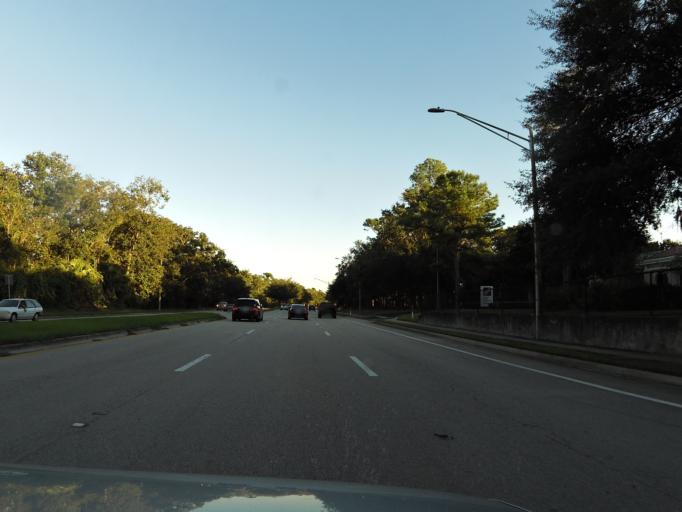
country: US
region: Florida
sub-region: Duval County
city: Jacksonville Beach
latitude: 30.2687
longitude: -81.4398
